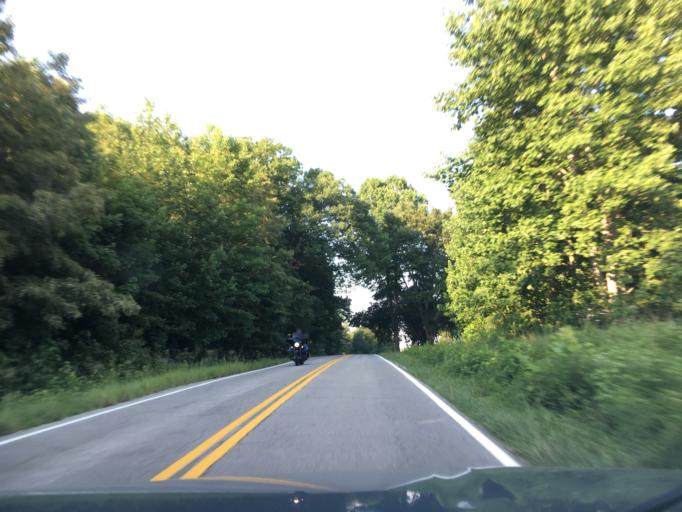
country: US
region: Virginia
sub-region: Pittsylvania County
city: Chatham
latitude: 36.8176
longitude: -79.2613
